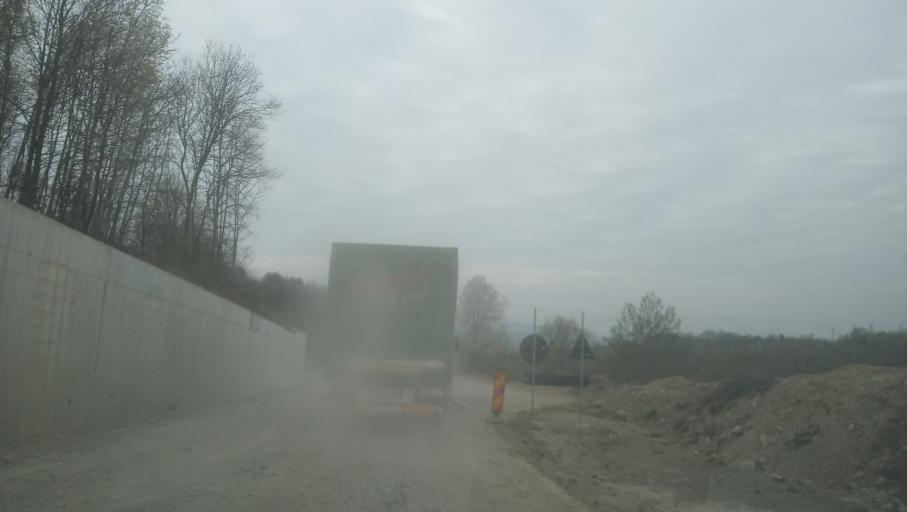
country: RO
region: Arad
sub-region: Comuna Varfurile
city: Varfurile
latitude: 46.3456
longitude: 22.5512
